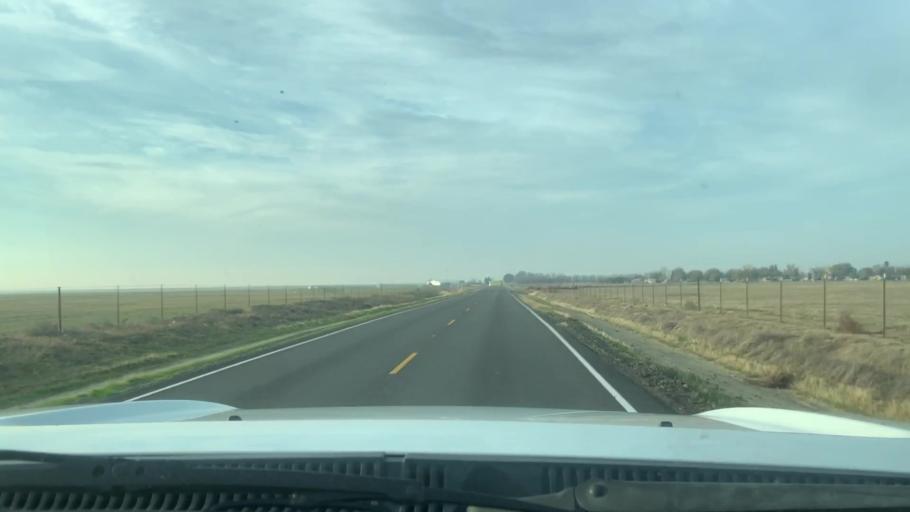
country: US
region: California
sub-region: Kern County
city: Lost Hills
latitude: 35.6060
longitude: -119.8567
